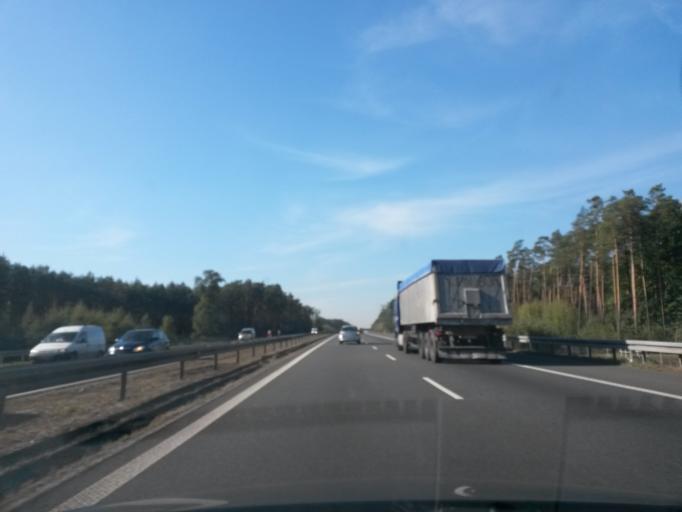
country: PL
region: Opole Voivodeship
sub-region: Powiat opolski
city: Komprachcice
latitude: 50.5944
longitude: 17.8030
